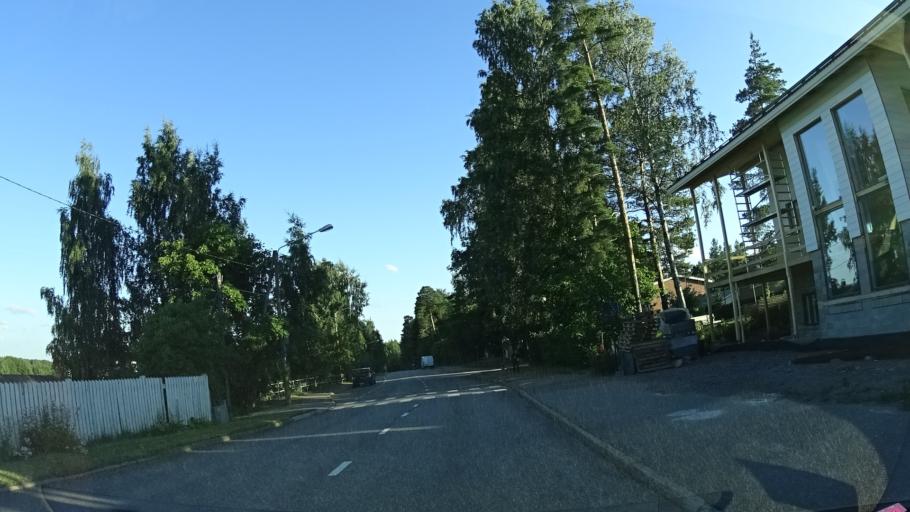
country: FI
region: Uusimaa
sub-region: Helsinki
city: Teekkarikylae
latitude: 60.2775
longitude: 24.8751
